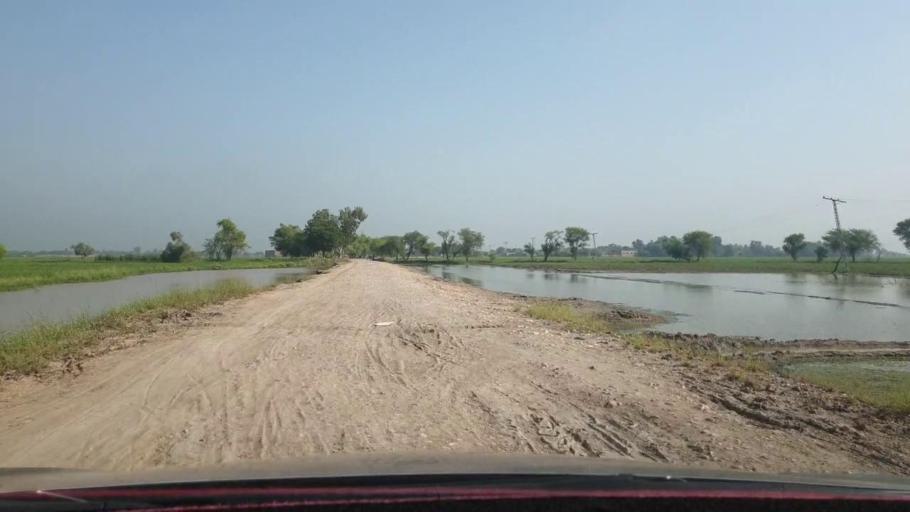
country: PK
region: Sindh
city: Nasirabad
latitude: 27.4564
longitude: 67.9177
